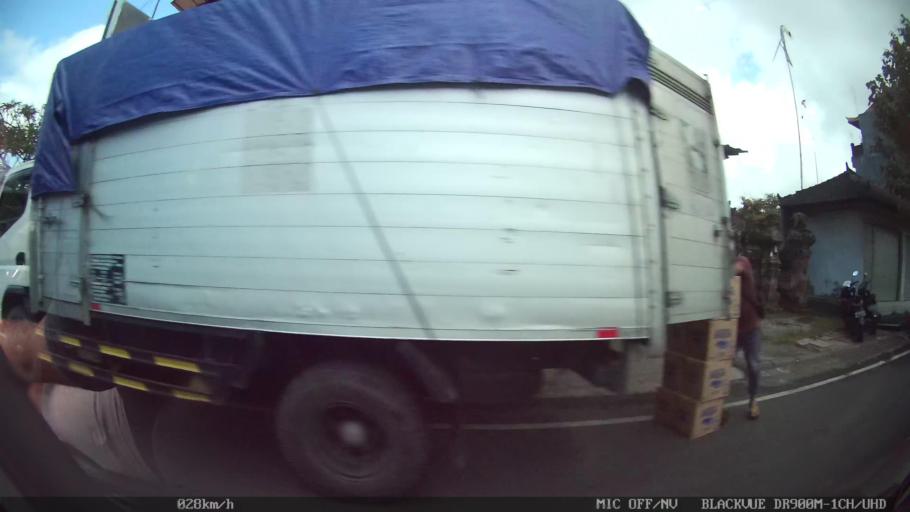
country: ID
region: Bali
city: Banjar Pasekan
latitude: -8.5982
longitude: 115.2846
